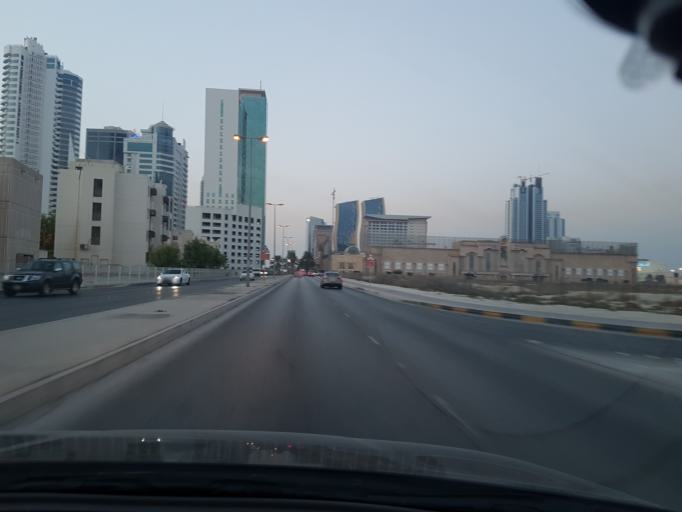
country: BH
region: Manama
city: Jidd Hafs
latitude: 26.2270
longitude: 50.5517
